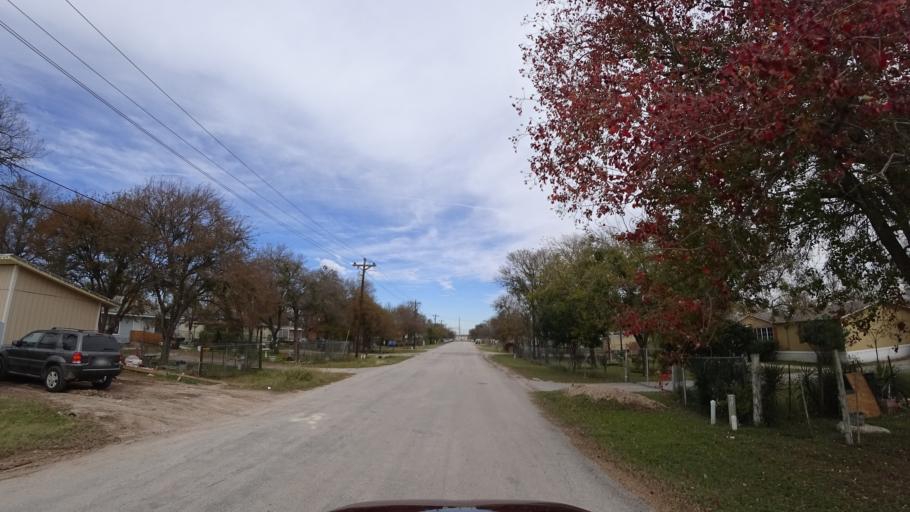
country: US
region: Texas
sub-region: Travis County
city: Garfield
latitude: 30.1359
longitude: -97.5632
